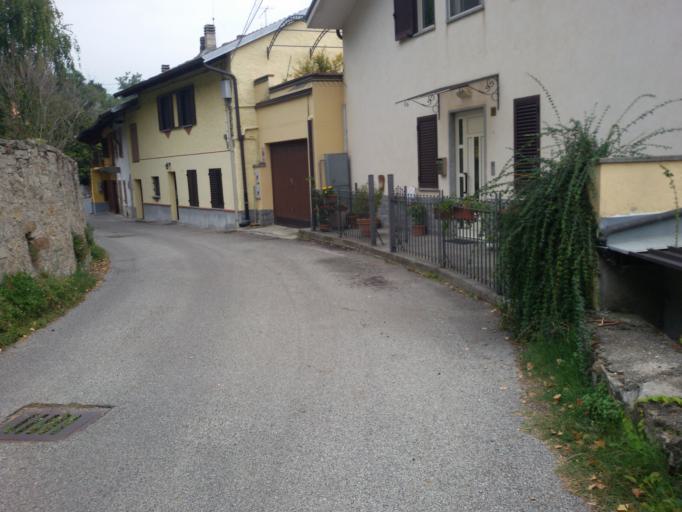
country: IT
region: Piedmont
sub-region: Provincia di Torino
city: Borgone Susa
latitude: 45.1253
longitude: 7.2376
